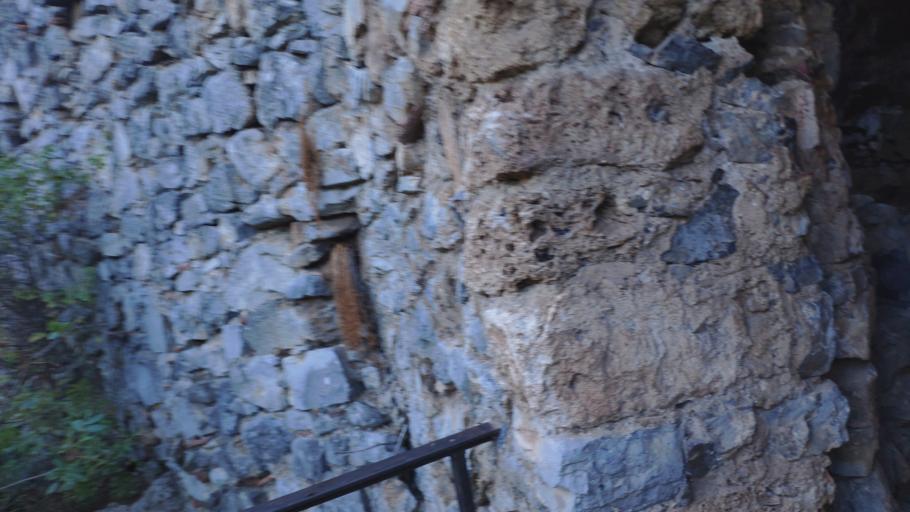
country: GR
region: Peloponnese
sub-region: Nomos Arkadias
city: Dimitsana
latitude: 37.5541
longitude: 22.0470
